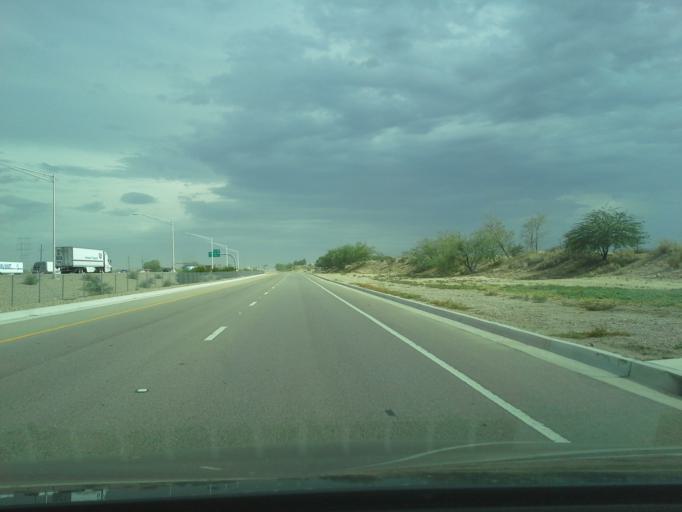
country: US
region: Arizona
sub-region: Pima County
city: Tortolita
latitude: 32.3729
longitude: -111.1049
